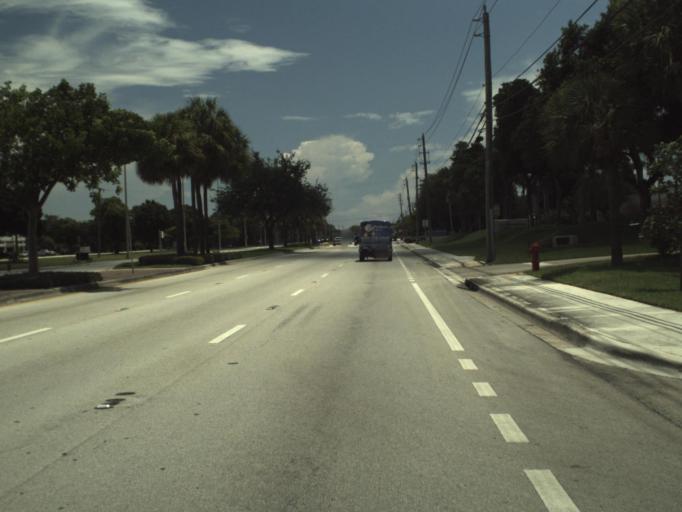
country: US
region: Florida
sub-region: Broward County
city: Twin Lakes
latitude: 26.1881
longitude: -80.1694
